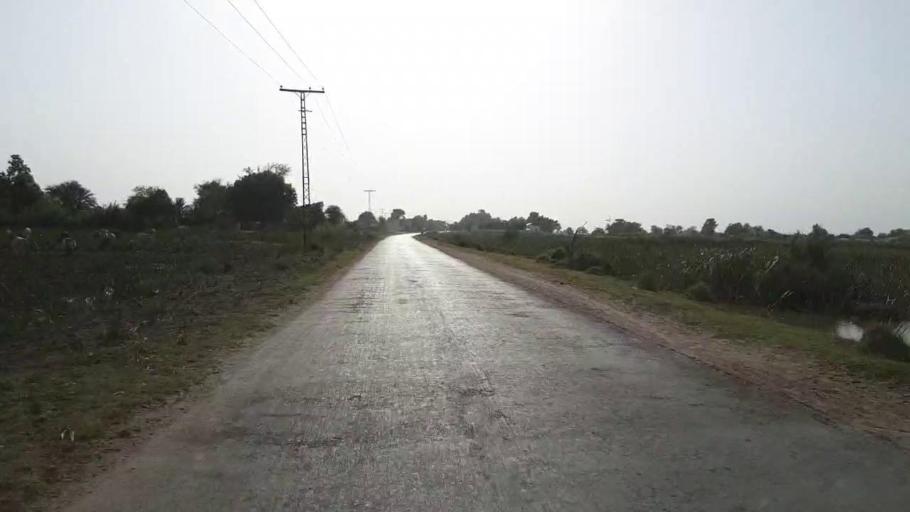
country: PK
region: Sindh
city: Jam Sahib
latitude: 26.3798
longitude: 68.8910
